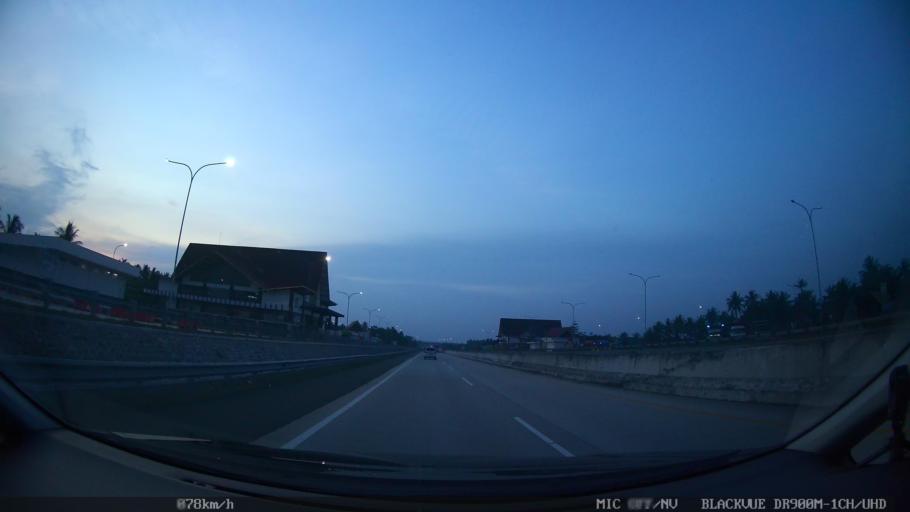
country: ID
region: Lampung
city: Kalianda
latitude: -5.6540
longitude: 105.5859
